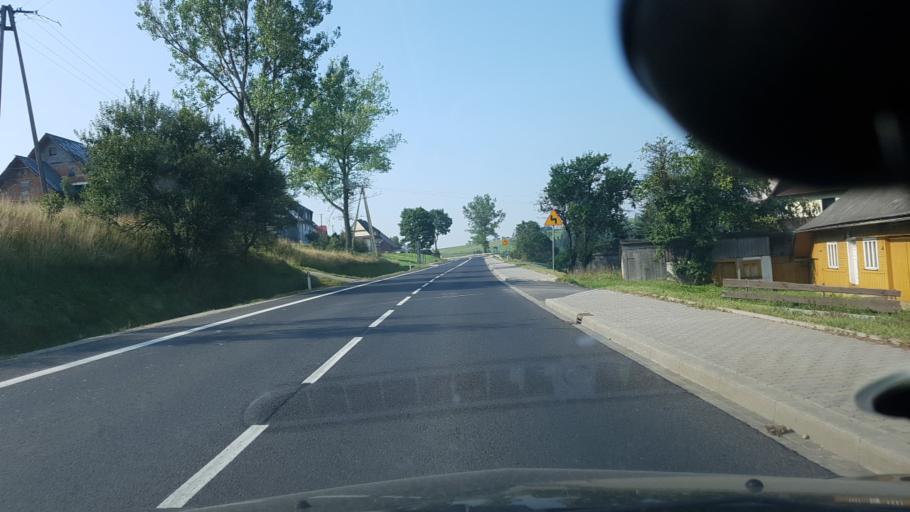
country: PL
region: Lesser Poland Voivodeship
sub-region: Powiat nowotarski
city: Podwilk
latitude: 49.5296
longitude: 19.7138
